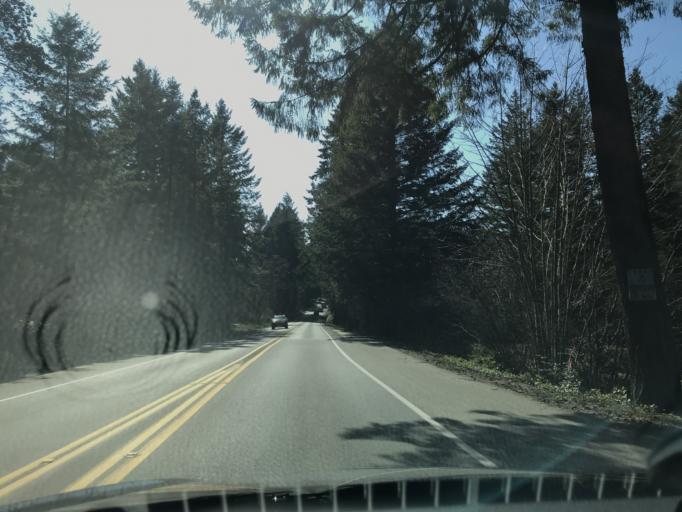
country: US
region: Washington
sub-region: Pierce County
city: Key Center
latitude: 47.3662
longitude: -122.7218
